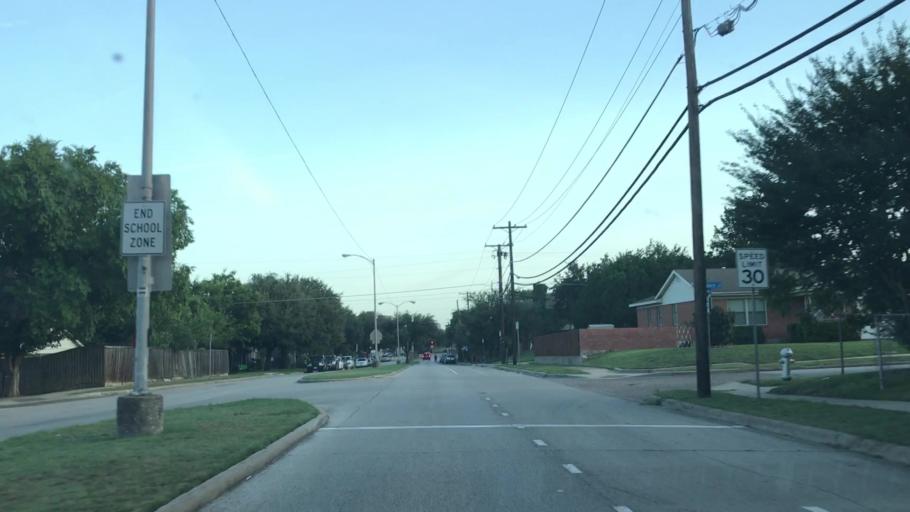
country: US
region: Texas
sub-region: Dallas County
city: Richardson
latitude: 32.9428
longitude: -96.7575
